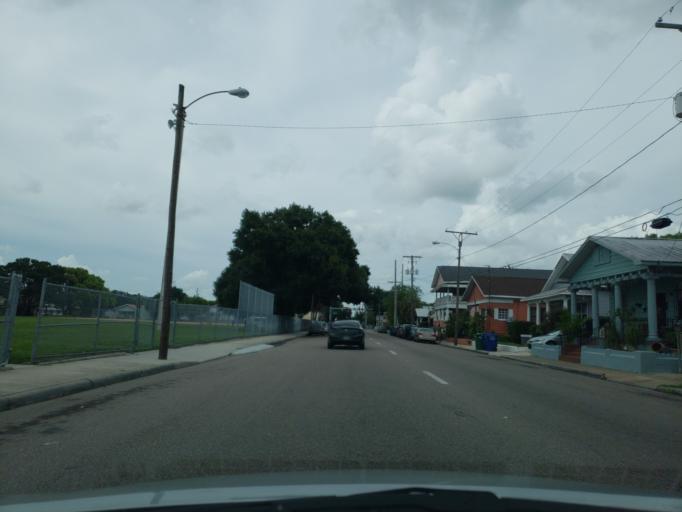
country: US
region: Florida
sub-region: Hillsborough County
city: Tampa
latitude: 27.9689
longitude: -82.4430
